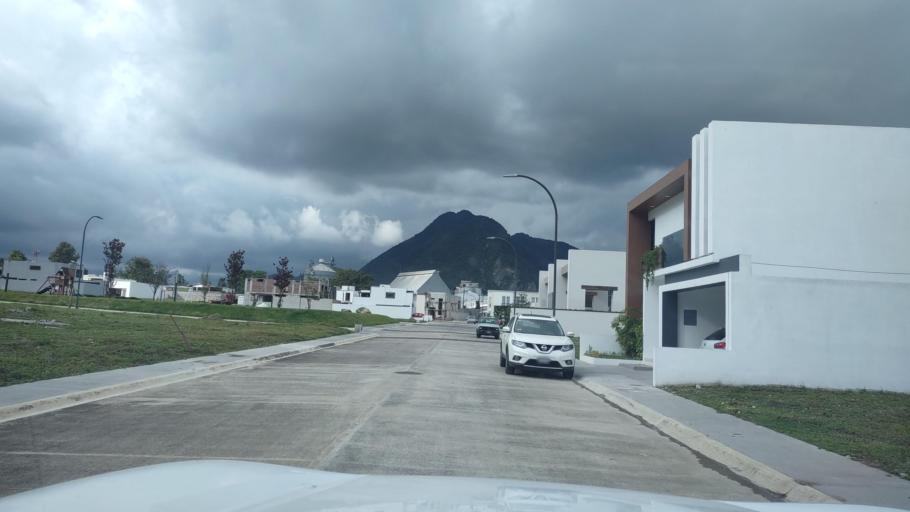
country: MX
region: Veracruz
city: Orizaba
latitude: 18.8419
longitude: -97.0879
